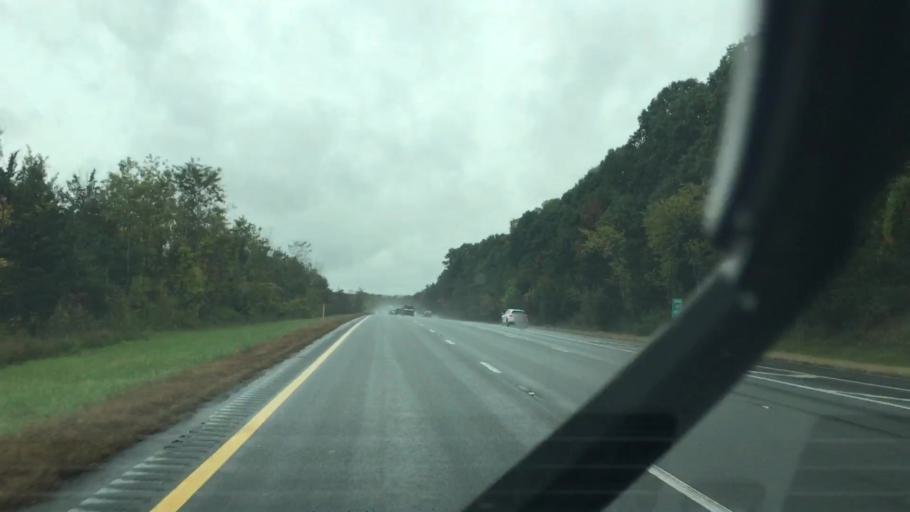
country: US
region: Massachusetts
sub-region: Essex County
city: Haverhill
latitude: 42.8034
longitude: -71.0556
